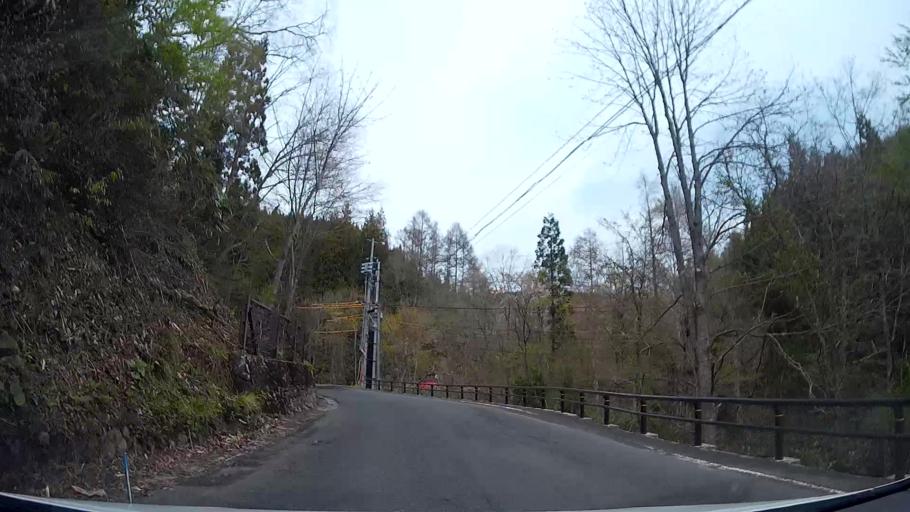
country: JP
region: Akita
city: Hanawa
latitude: 40.3806
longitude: 140.8913
